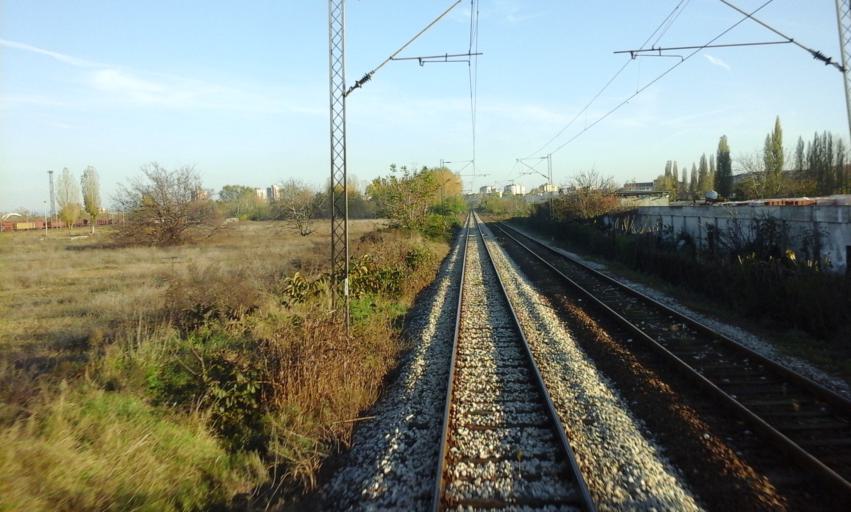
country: RS
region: Autonomna Pokrajina Vojvodina
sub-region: Juznobacki Okrug
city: Novi Sad
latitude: 45.2699
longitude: 19.8116
